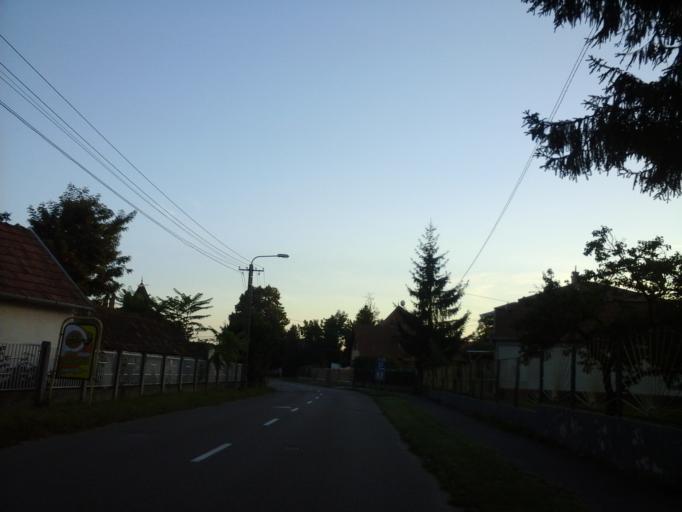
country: HU
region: Hajdu-Bihar
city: Hajduszoboszlo
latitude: 47.4595
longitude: 21.4124
